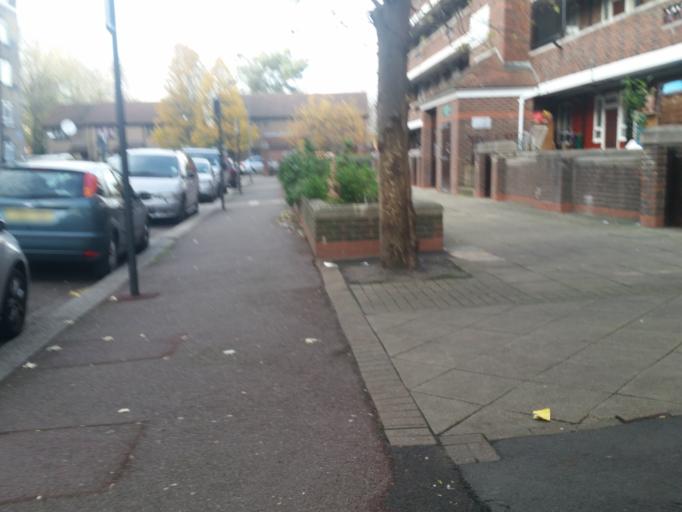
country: GB
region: England
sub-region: Greater London
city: Hammersmith
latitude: 51.5131
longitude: -0.2302
